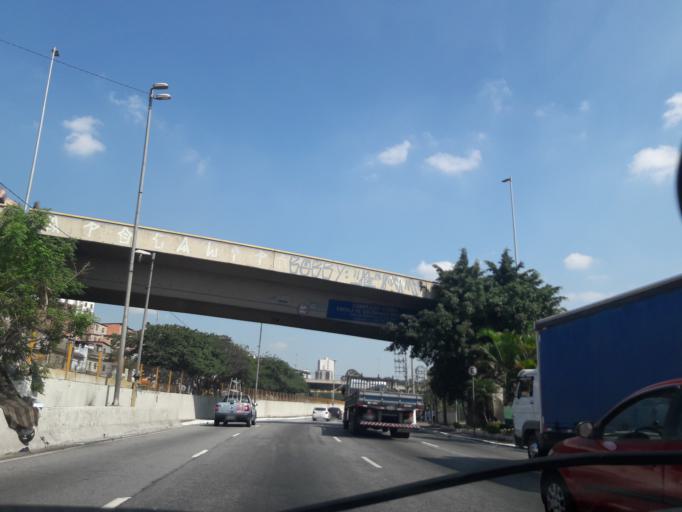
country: BR
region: Sao Paulo
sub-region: Sao Caetano Do Sul
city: Sao Caetano do Sul
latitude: -23.5998
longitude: -46.5978
